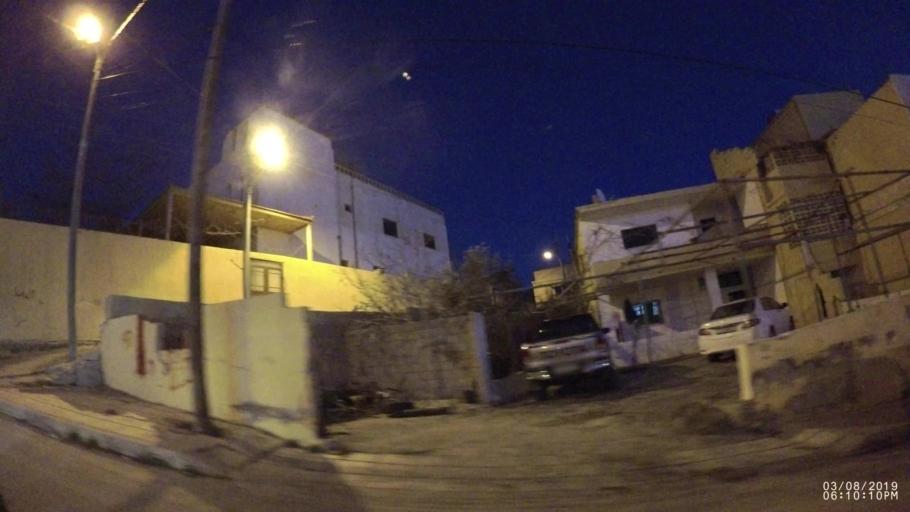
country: JO
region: Ma'an
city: Petra
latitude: 30.3292
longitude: 35.4838
